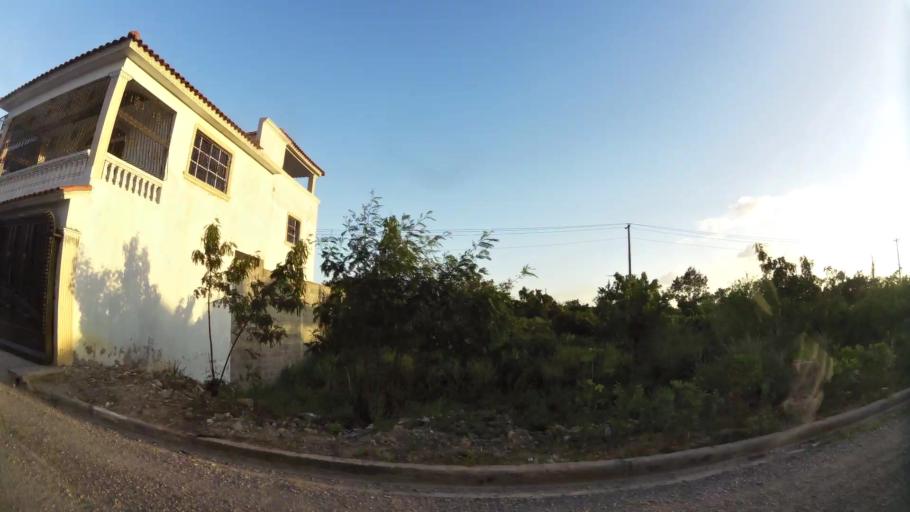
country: DO
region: Santo Domingo
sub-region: Santo Domingo
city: Santo Domingo Este
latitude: 18.4867
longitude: -69.8172
